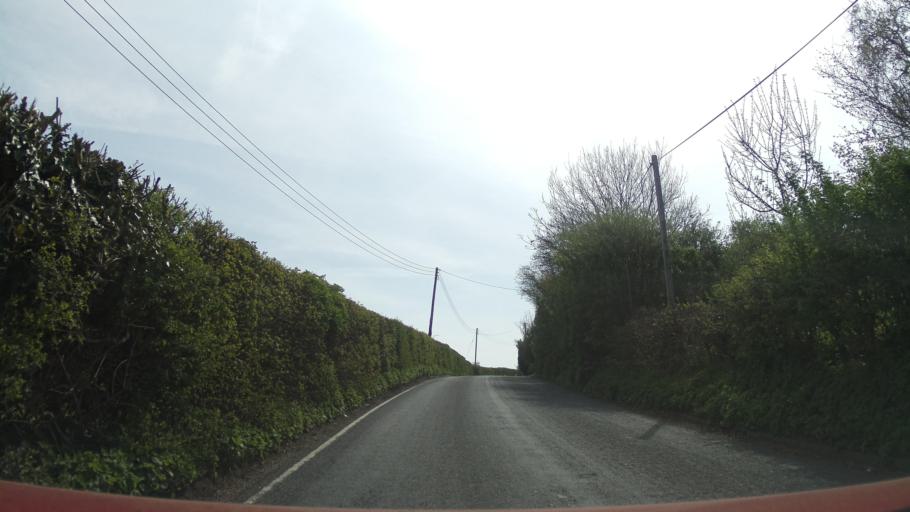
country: GB
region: England
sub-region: Somerset
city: Street
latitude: 51.1216
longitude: -2.7969
